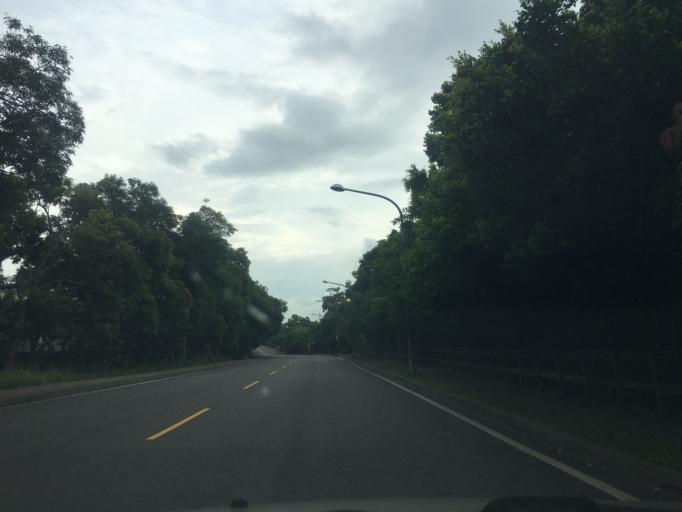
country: TW
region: Taiwan
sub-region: Changhua
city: Chang-hua
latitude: 24.0699
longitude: 120.5650
